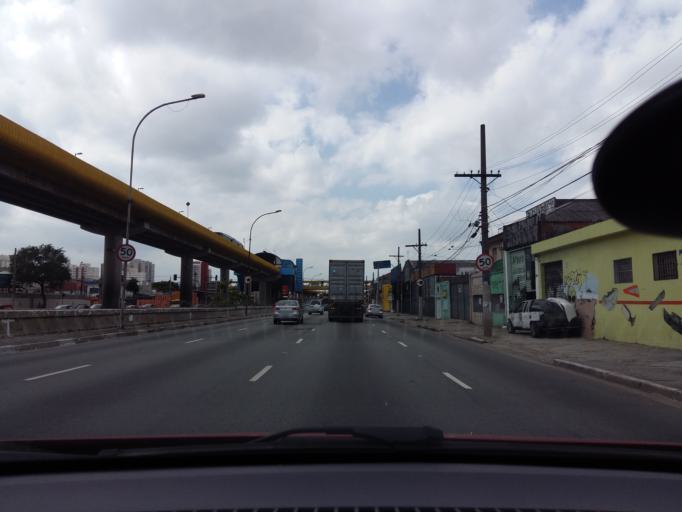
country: BR
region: Sao Paulo
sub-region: Sao Caetano Do Sul
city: Sao Caetano do Sul
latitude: -23.5934
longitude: -46.5974
